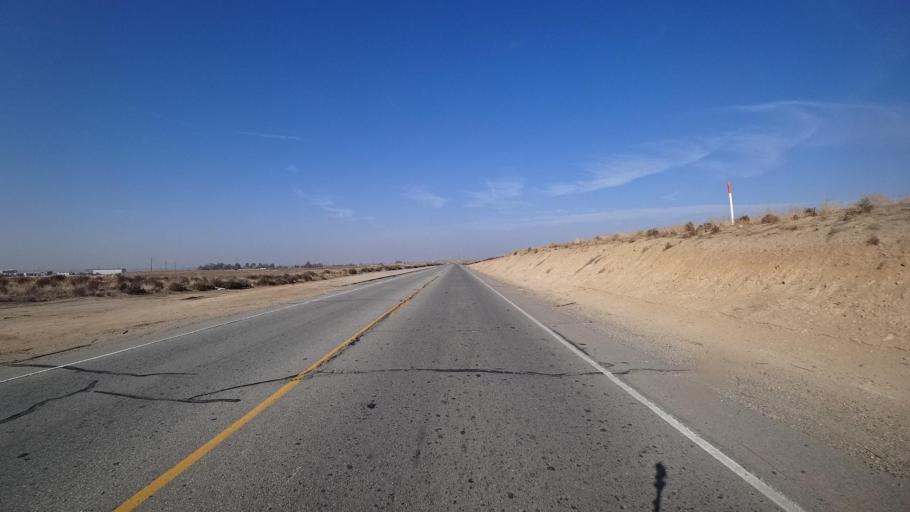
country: US
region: California
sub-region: Kern County
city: Oildale
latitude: 35.4717
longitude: -119.0687
